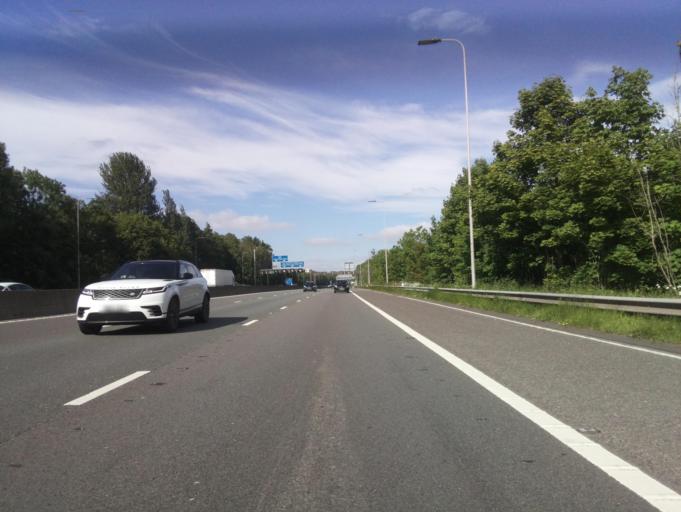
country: GB
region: England
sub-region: City and Borough of Salford
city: Walkden
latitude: 53.5033
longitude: -2.3812
